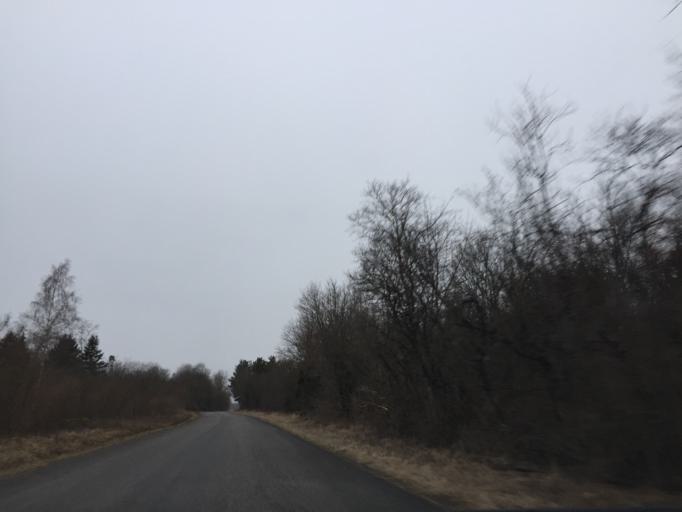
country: EE
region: Laeaene
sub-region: Lihula vald
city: Lihula
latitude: 58.6440
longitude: 23.6271
